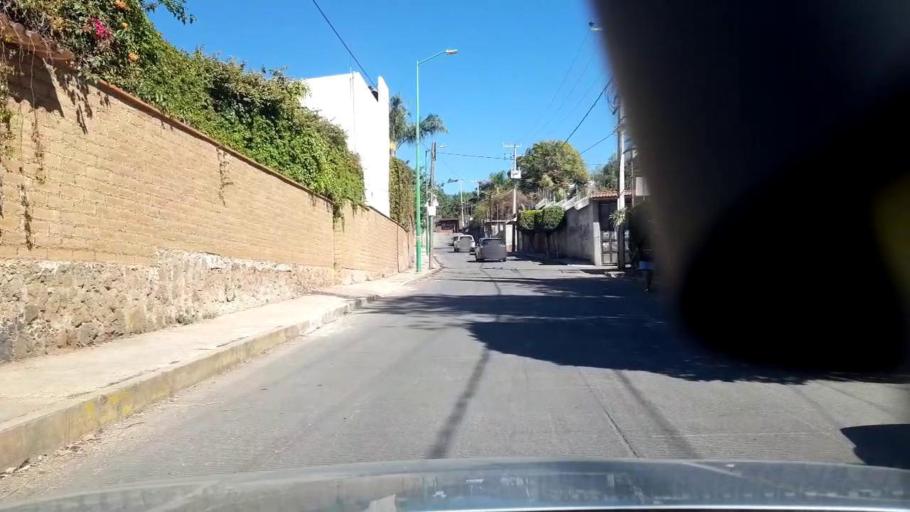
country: MX
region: Morelos
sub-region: Cuernavaca
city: Colonia los Cerritos
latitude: 18.9658
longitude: -99.2228
